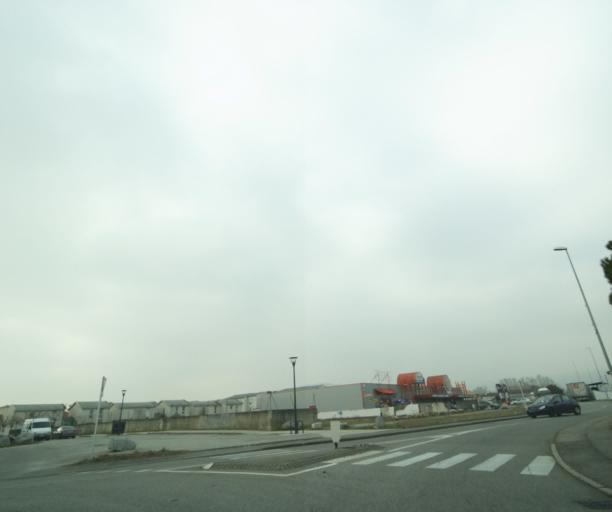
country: FR
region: Rhone-Alpes
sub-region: Departement de la Drome
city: Bourg-les-Valence
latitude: 44.9584
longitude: 4.8840
